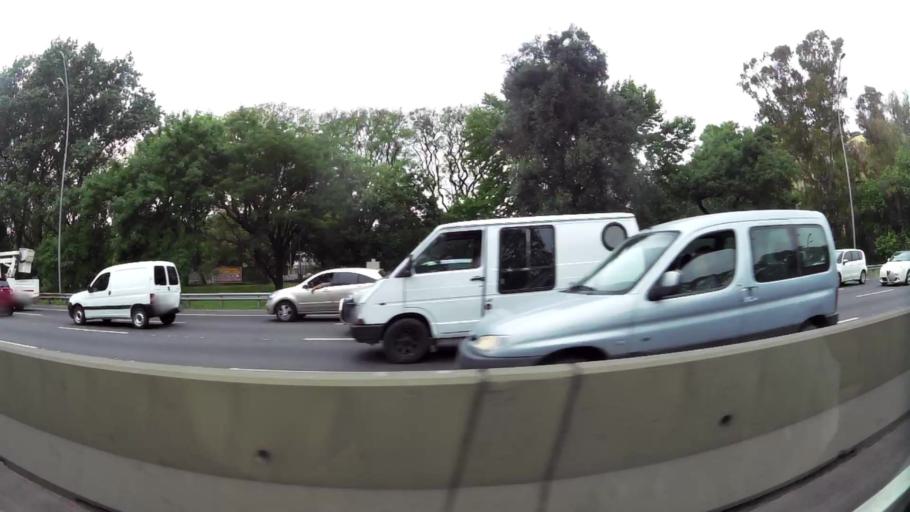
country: AR
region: Buenos Aires
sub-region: Partido de General San Martin
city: General San Martin
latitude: -34.5778
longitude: -58.5133
